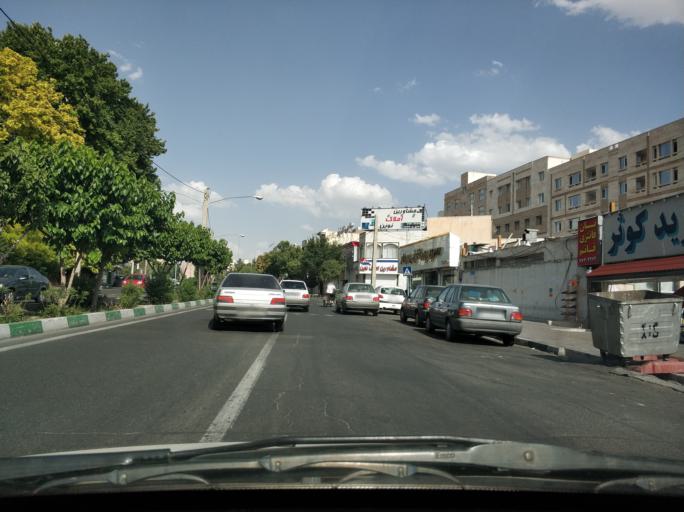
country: IR
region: Tehran
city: Tehran
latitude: 35.7420
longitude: 51.5863
